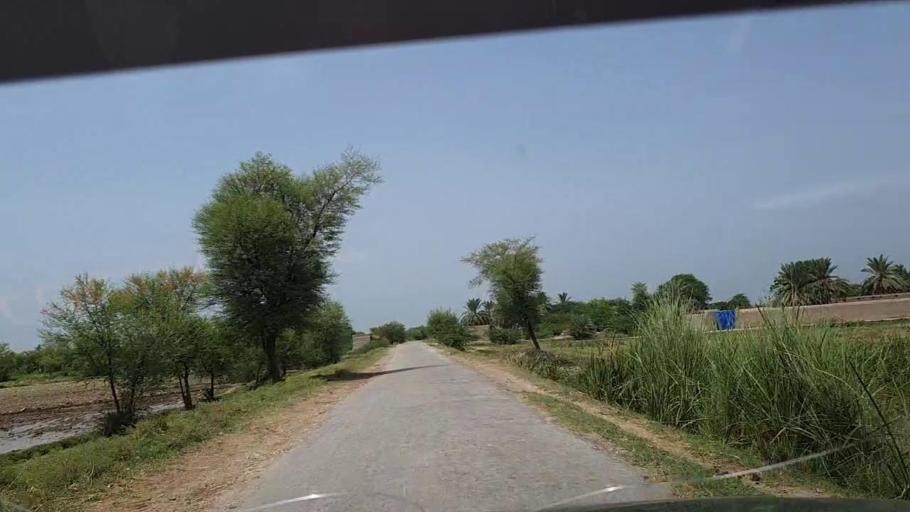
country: PK
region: Sindh
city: Khanpur
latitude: 27.7984
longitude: 69.4523
